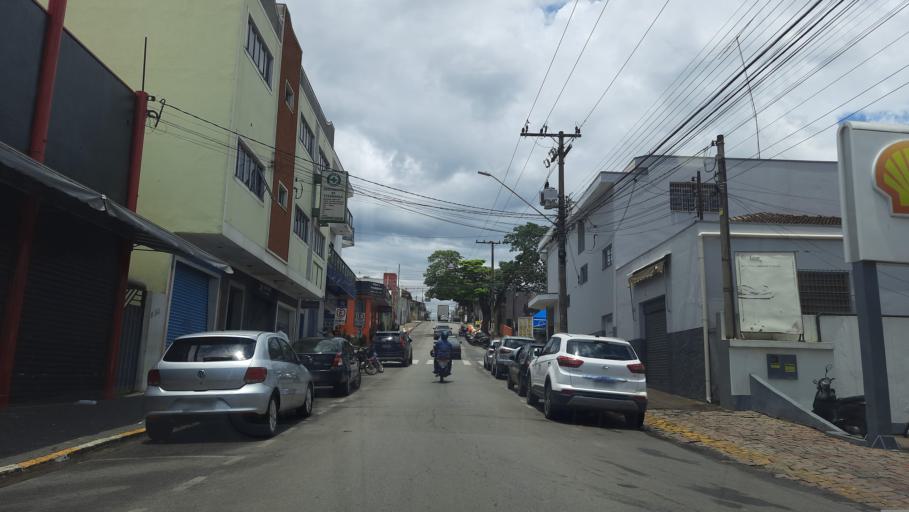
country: BR
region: Sao Paulo
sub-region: Vargem Grande Do Sul
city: Vargem Grande do Sul
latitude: -21.8344
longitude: -46.8953
